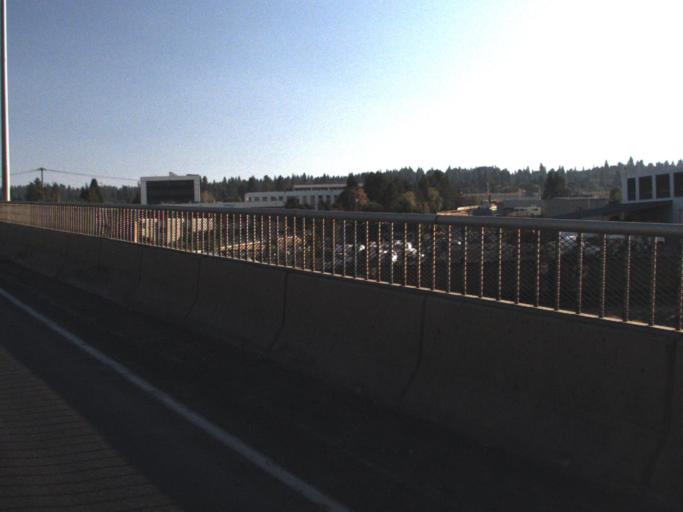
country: US
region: Washington
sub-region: Spokane County
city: Spokane
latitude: 47.6587
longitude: -117.3956
